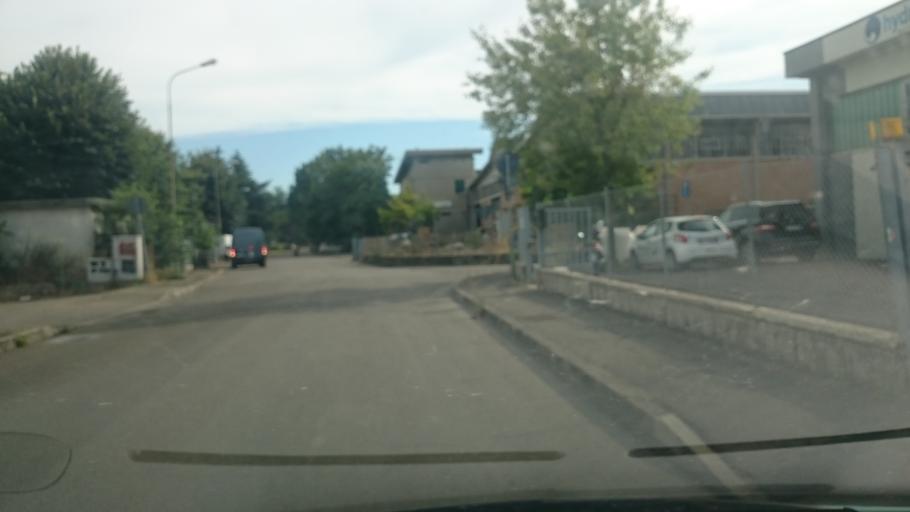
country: IT
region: Emilia-Romagna
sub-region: Provincia di Reggio Emilia
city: Forche
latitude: 44.6699
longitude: 10.5975
